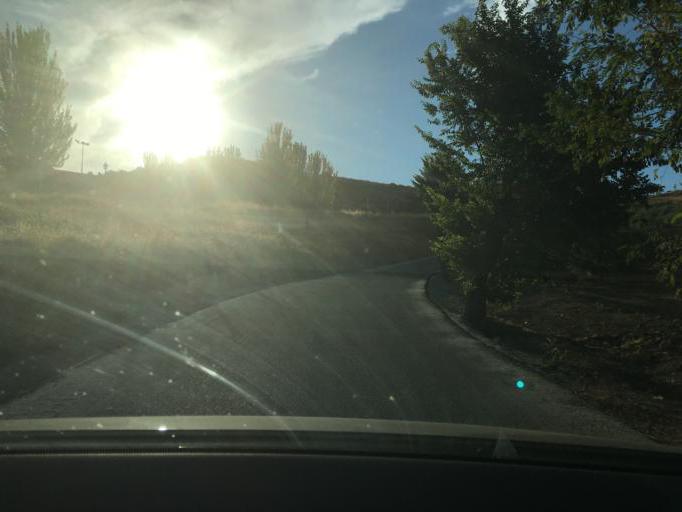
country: ES
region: Andalusia
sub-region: Provincia de Granada
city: Beas de Granada
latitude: 37.2148
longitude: -3.4808
